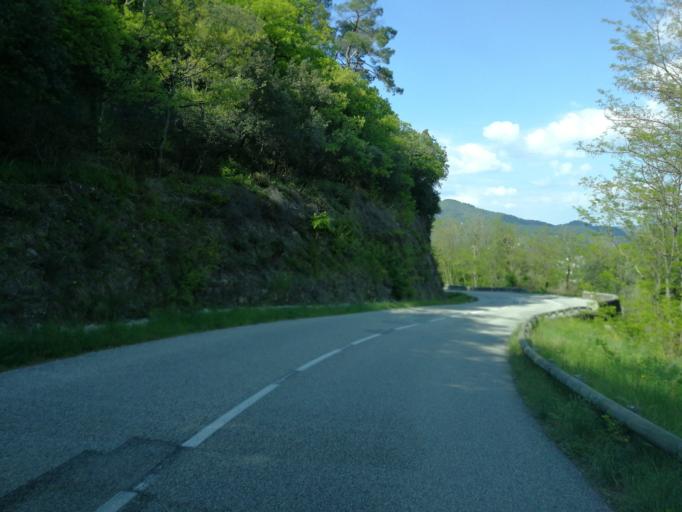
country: FR
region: Rhone-Alpes
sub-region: Departement de l'Ardeche
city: Saint-Sauveur-de-Montagut
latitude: 44.7953
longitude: 4.6144
